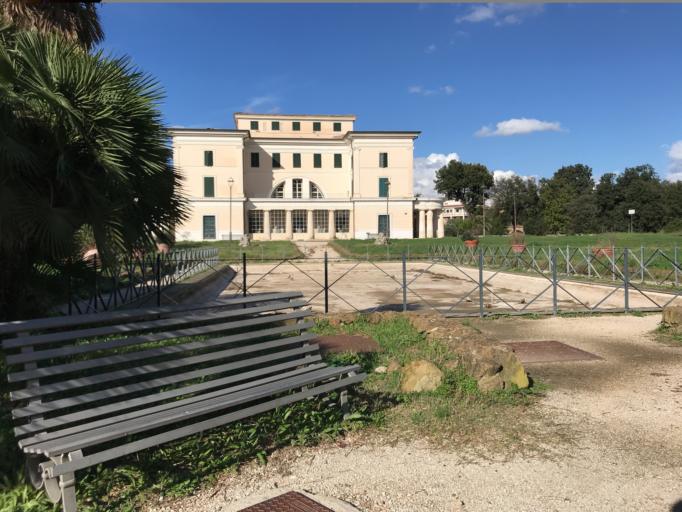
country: IT
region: Latium
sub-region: Citta metropolitana di Roma Capitale
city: Rome
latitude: 41.9141
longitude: 12.5114
